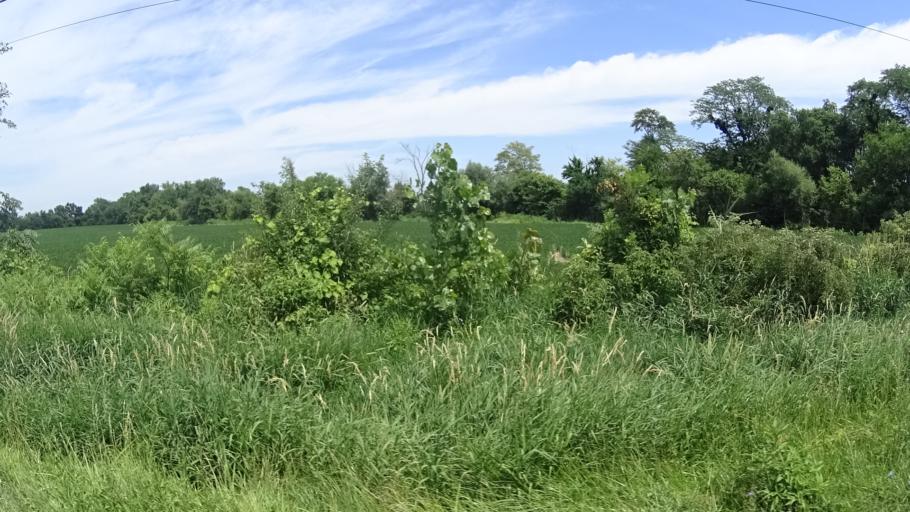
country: US
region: Ohio
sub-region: Erie County
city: Sandusky
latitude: 41.3921
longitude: -82.7708
